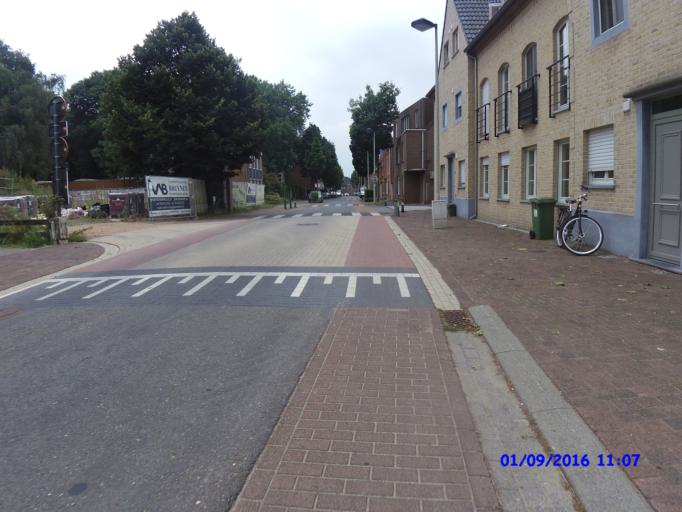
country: BE
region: Flanders
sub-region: Provincie Antwerpen
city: Beerse
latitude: 51.3224
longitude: 4.8589
